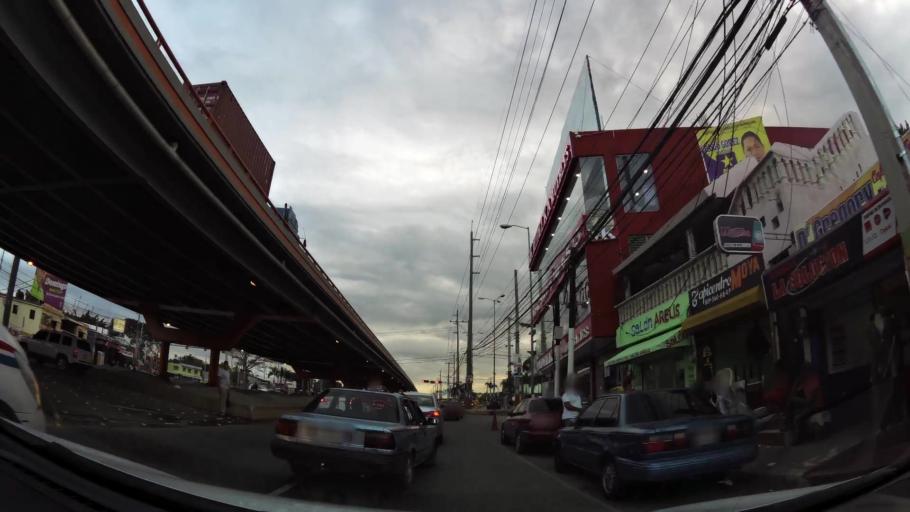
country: DO
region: Santo Domingo
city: Santo Domingo Oeste
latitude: 18.5220
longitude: -70.0106
